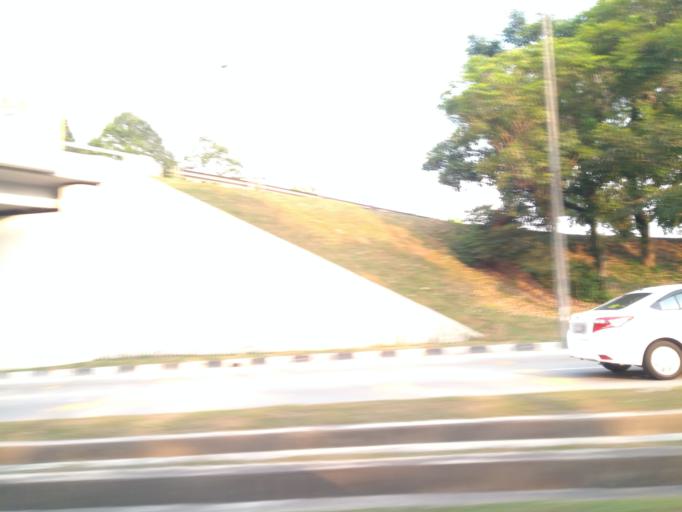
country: MY
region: Kuala Lumpur
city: Kuala Lumpur
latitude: 3.1163
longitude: 101.7071
